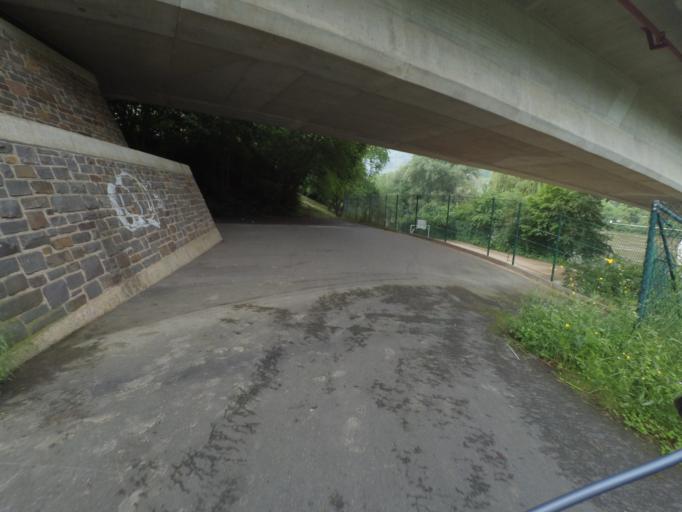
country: DE
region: Rheinland-Pfalz
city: Cochem
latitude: 50.1548
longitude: 7.1718
